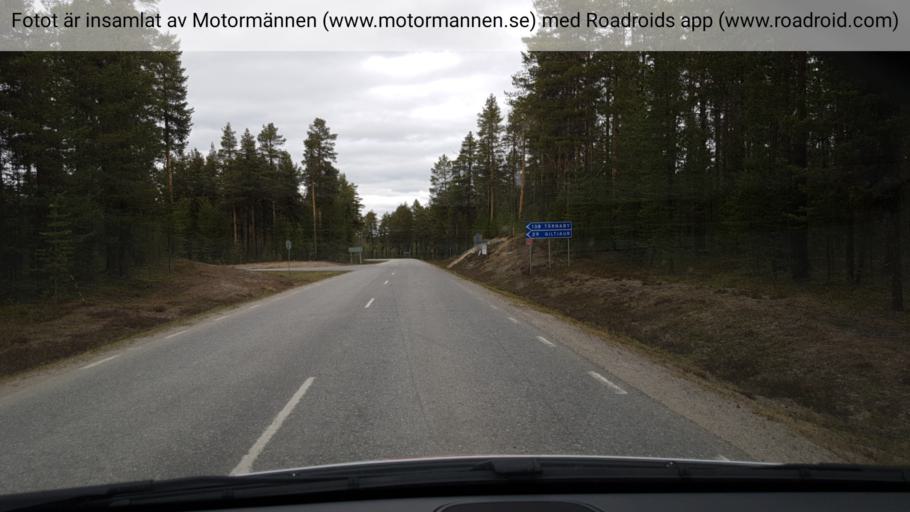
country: SE
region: Vaesterbotten
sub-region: Sorsele Kommun
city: Sorsele
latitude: 65.5485
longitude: 17.5096
